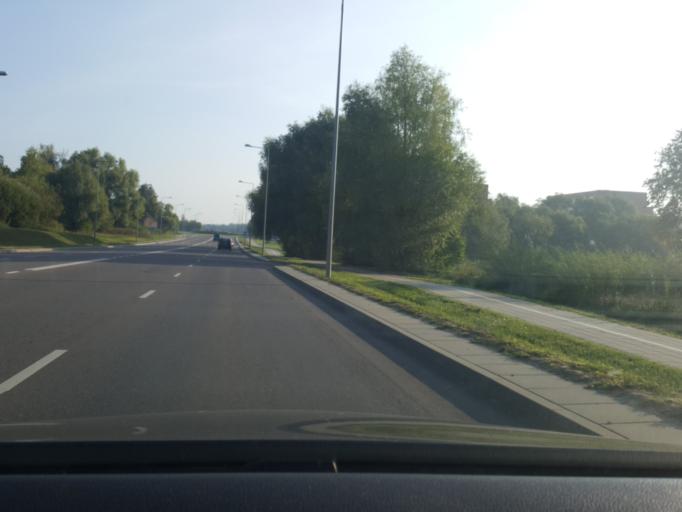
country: LT
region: Alytaus apskritis
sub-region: Alytus
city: Alytus
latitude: 54.4217
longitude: 24.0299
